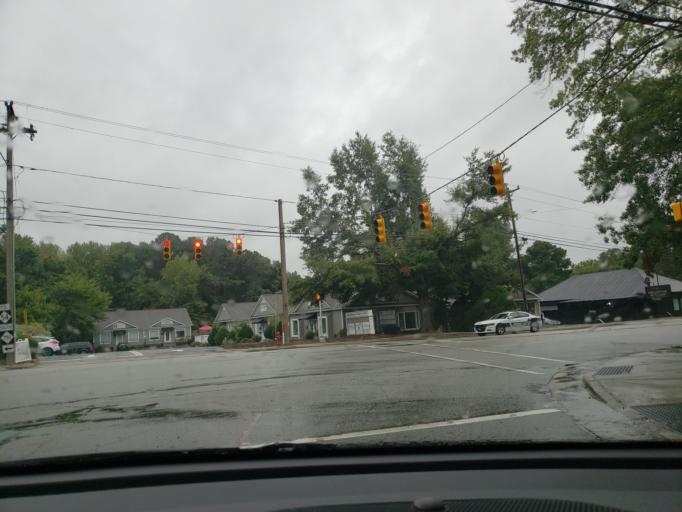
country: US
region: North Carolina
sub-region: Durham County
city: Durham
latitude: 35.9676
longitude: -78.9440
